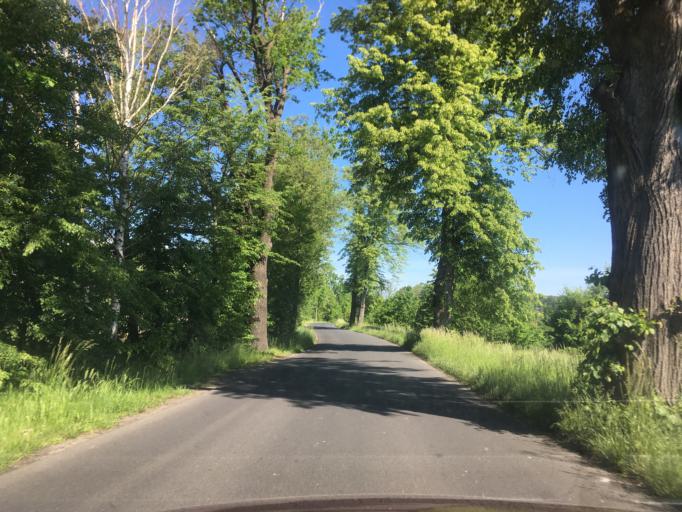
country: PL
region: Lower Silesian Voivodeship
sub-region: Powiat zgorzelecki
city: Sulikow
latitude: 51.1077
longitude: 15.0348
